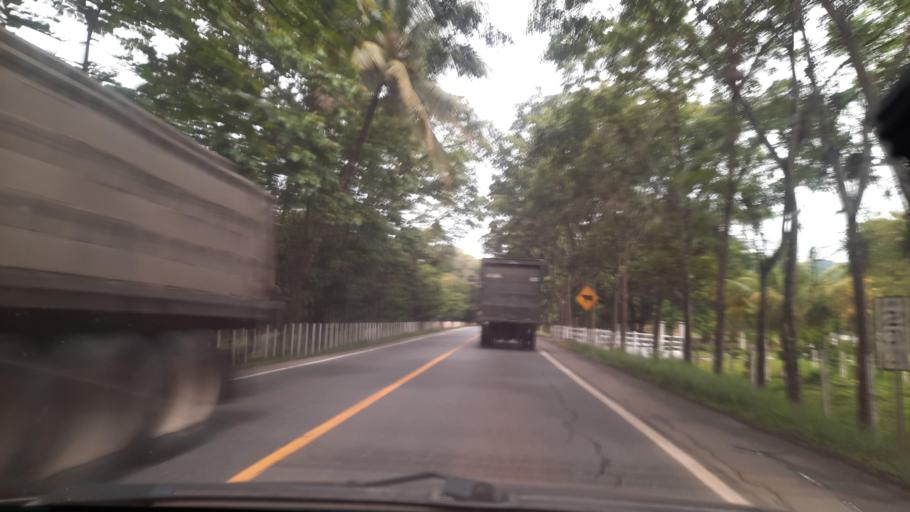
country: GT
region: Izabal
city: Morales
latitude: 15.4638
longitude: -88.9197
